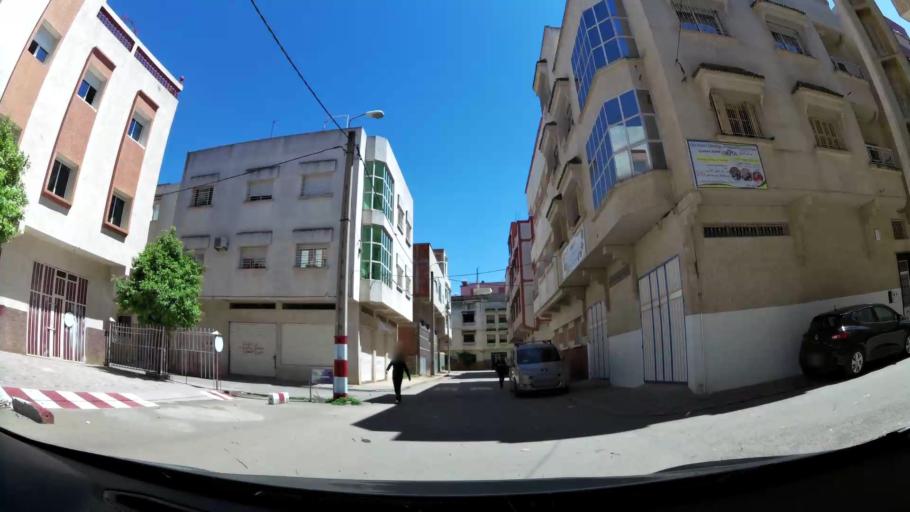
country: MA
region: Meknes-Tafilalet
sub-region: Meknes
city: Meknes
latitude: 33.8962
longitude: -5.5796
